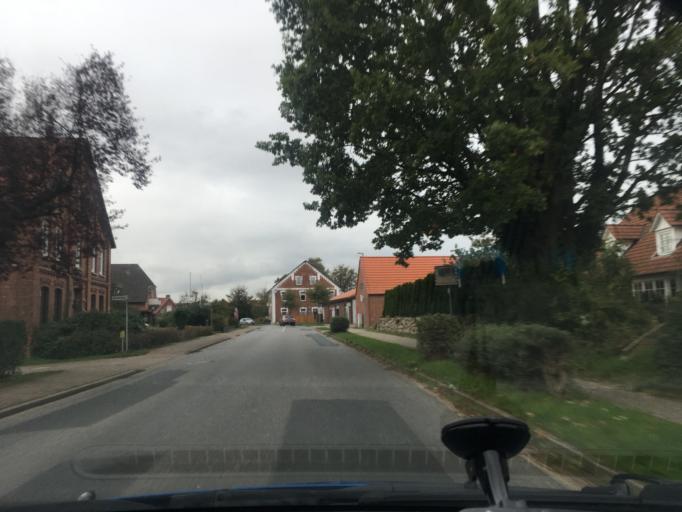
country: DE
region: Lower Saxony
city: Marschacht
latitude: 53.4138
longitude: 10.3804
